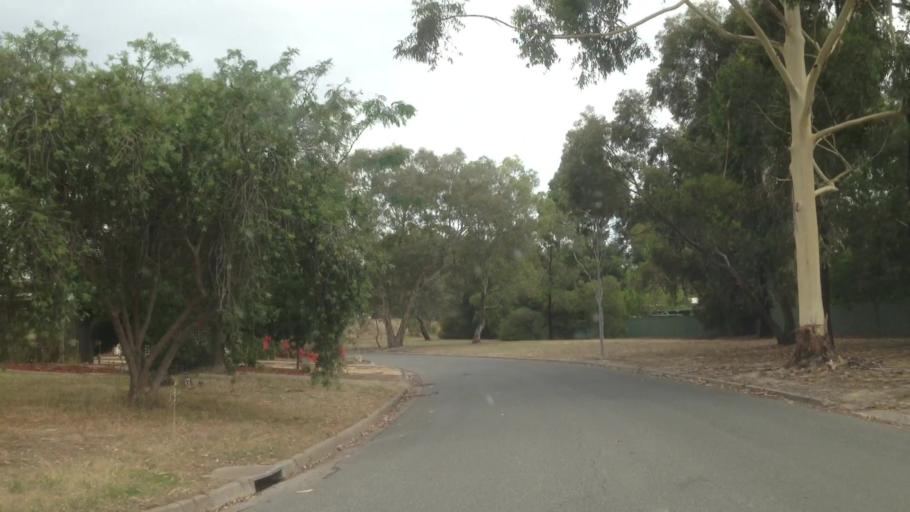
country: AU
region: South Australia
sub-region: Barossa
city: Williamstown
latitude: -34.6700
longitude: 138.8799
